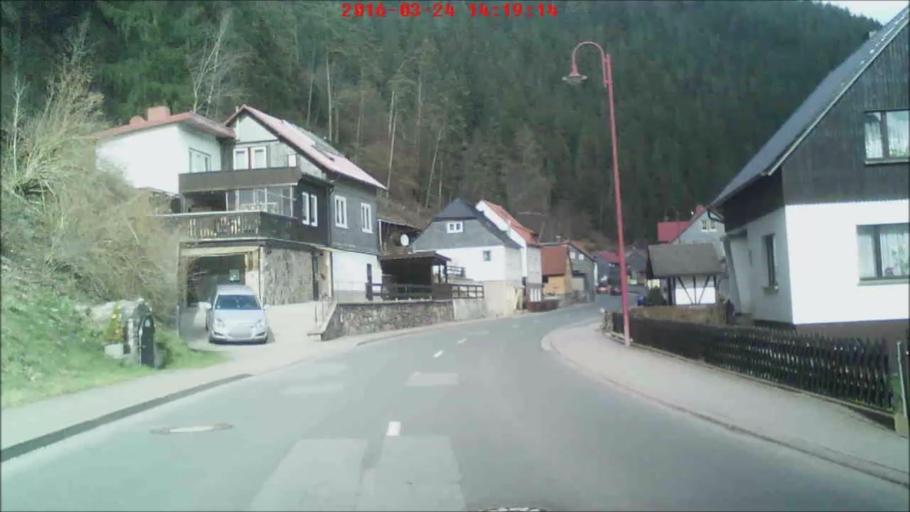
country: DE
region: Thuringia
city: Mellenbach-Glasbach
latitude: 50.6069
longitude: 11.1129
